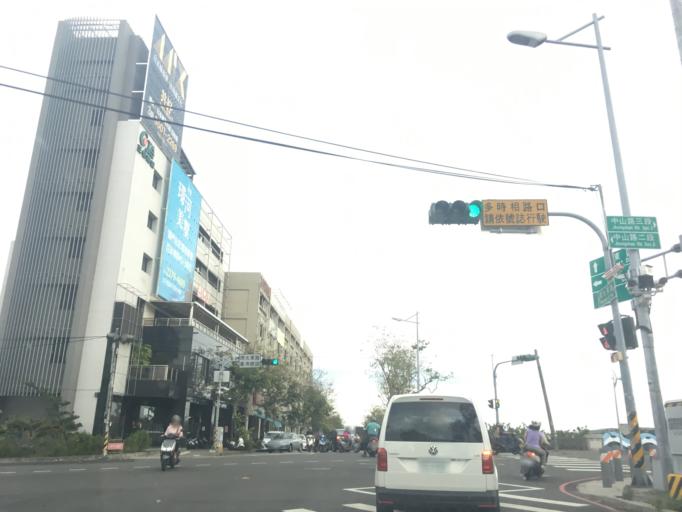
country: TW
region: Taiwan
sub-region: Taichung City
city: Taichung
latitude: 24.1499
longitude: 120.7246
